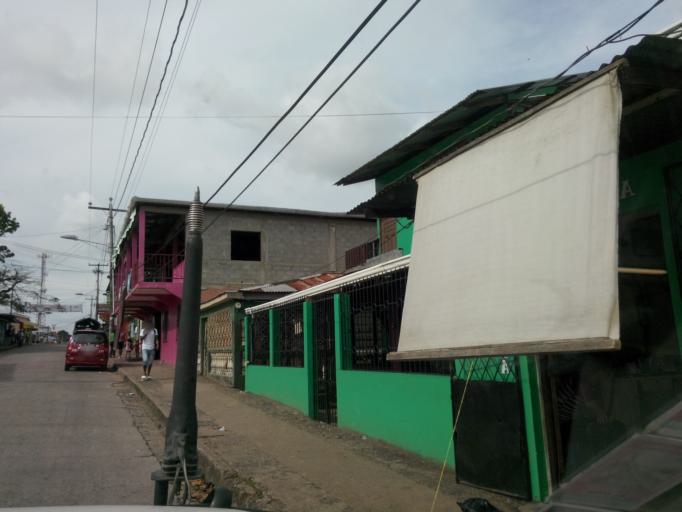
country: NI
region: Atlantico Sur
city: Bluefields
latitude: 12.0104
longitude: -83.7631
